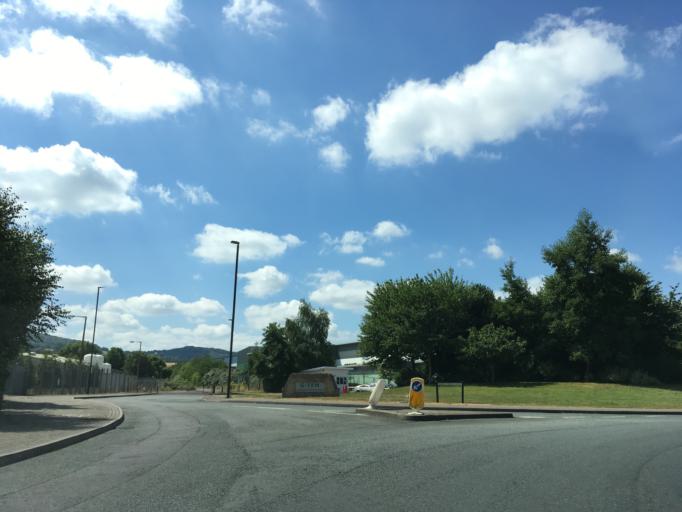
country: GB
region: England
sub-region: Gloucestershire
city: Churchdown
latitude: 51.8468
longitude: -2.1681
